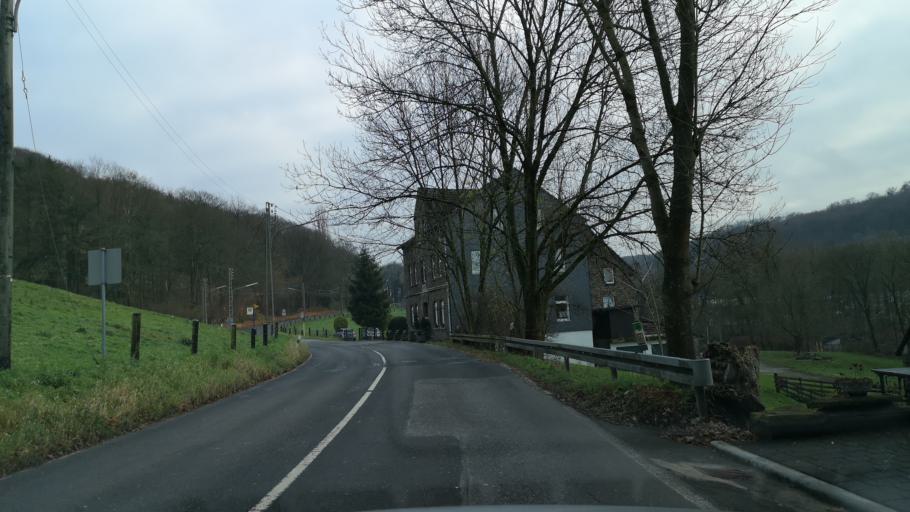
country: DE
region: North Rhine-Westphalia
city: Hattingen
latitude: 51.3792
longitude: 7.1250
